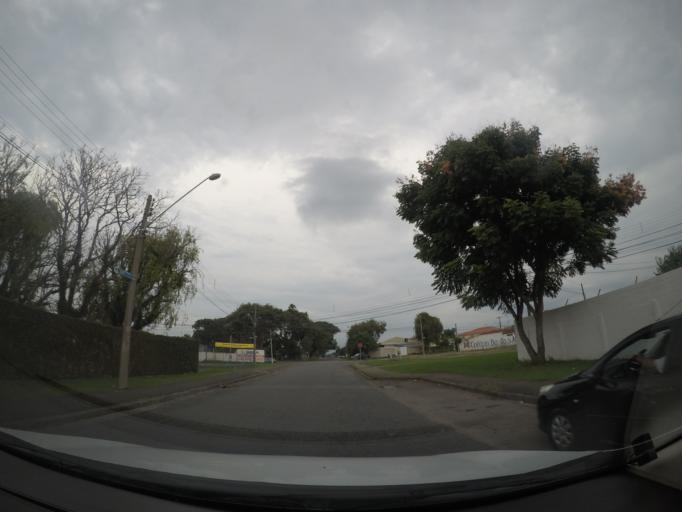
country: BR
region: Parana
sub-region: Sao Jose Dos Pinhais
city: Sao Jose dos Pinhais
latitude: -25.5104
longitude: -49.2288
